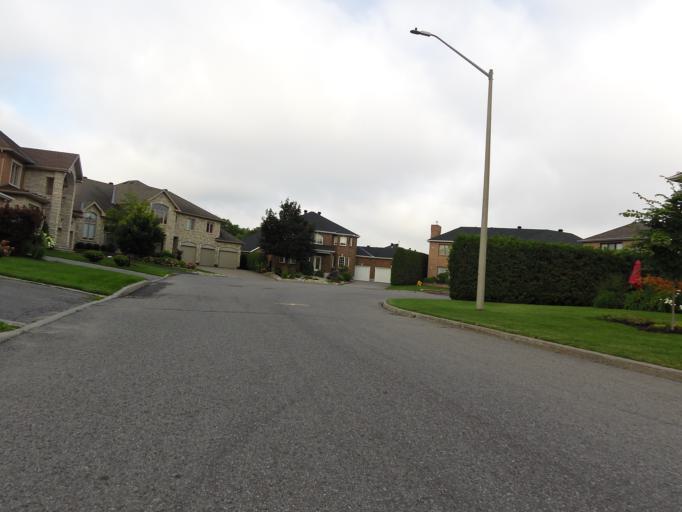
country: CA
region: Ontario
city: Ottawa
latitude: 45.3461
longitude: -75.6570
